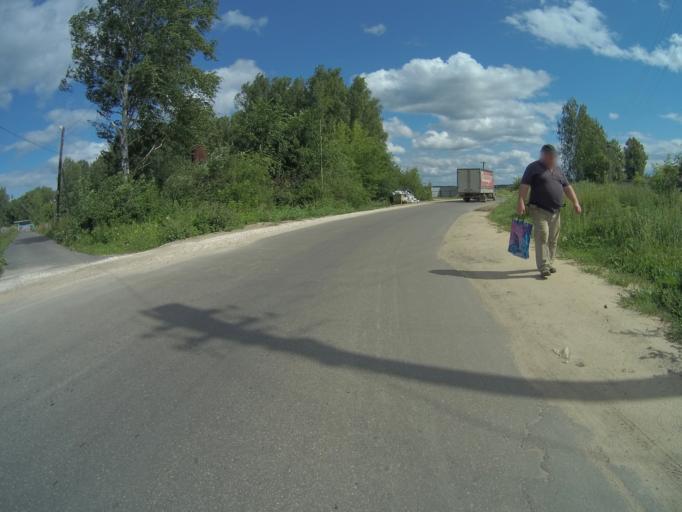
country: RU
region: Vladimir
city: Vorsha
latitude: 56.0609
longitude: 40.1855
